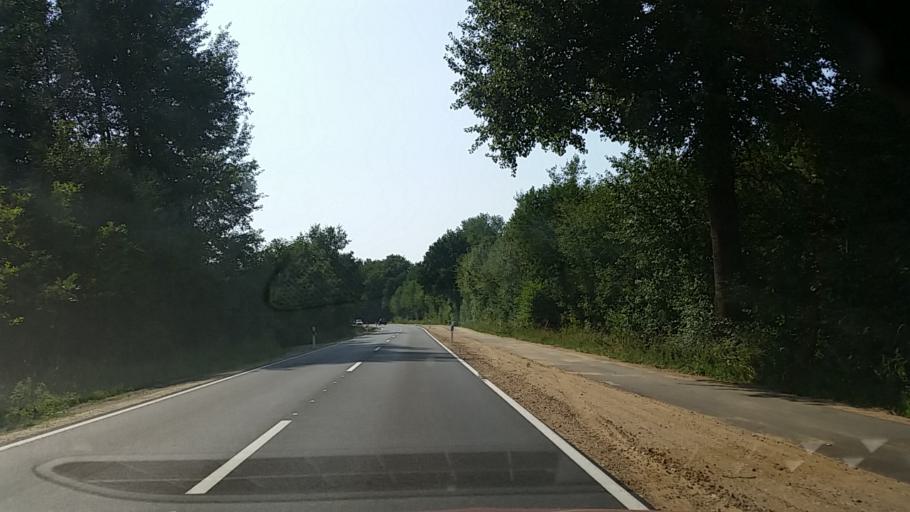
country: DE
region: Schleswig-Holstein
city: Witzhave
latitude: 53.5652
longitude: 10.3171
